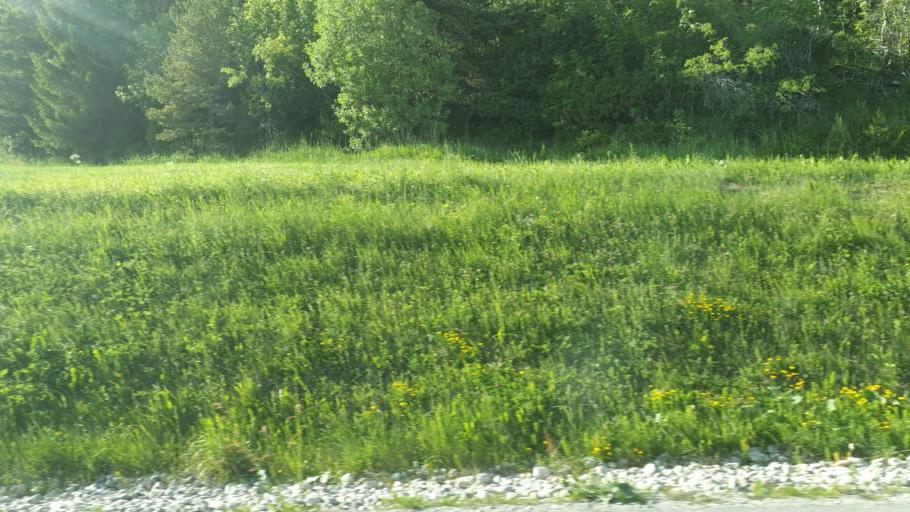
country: NO
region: Sor-Trondelag
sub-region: Rissa
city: Rissa
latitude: 63.4985
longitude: 10.1125
